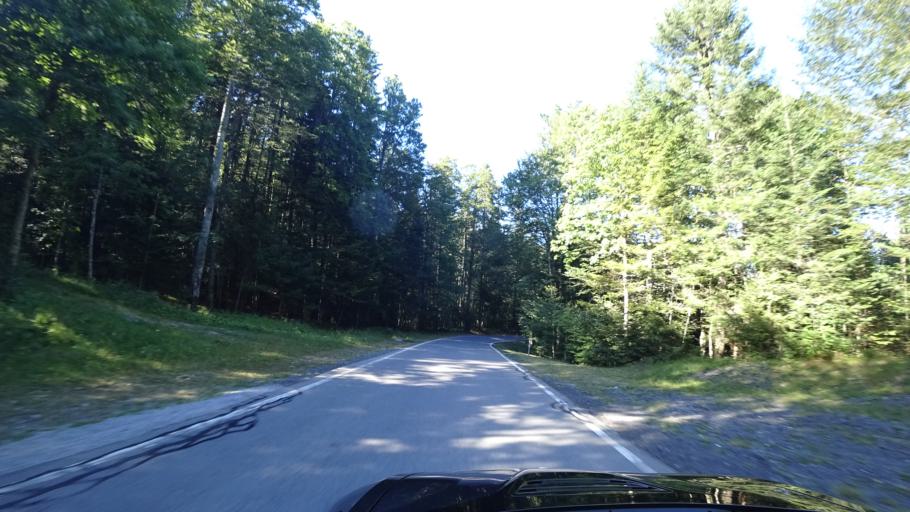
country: CH
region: Obwalden
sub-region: Obwalden
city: Lungern
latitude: 46.8295
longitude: 8.1241
